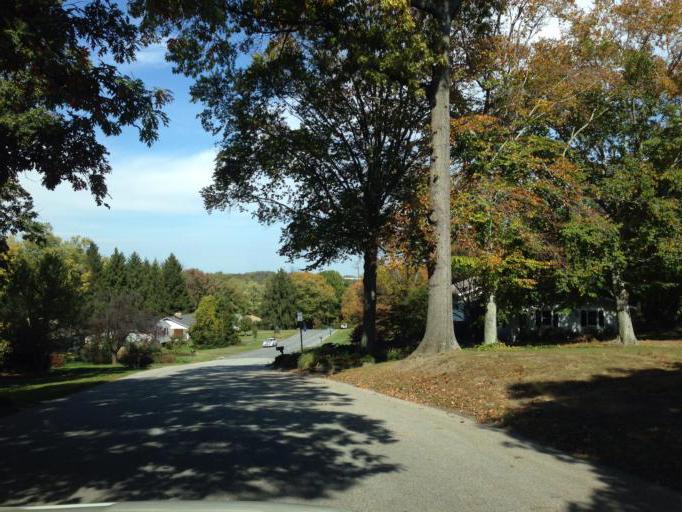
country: US
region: Maryland
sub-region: Howard County
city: Ellicott City
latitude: 39.2684
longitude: -76.8241
